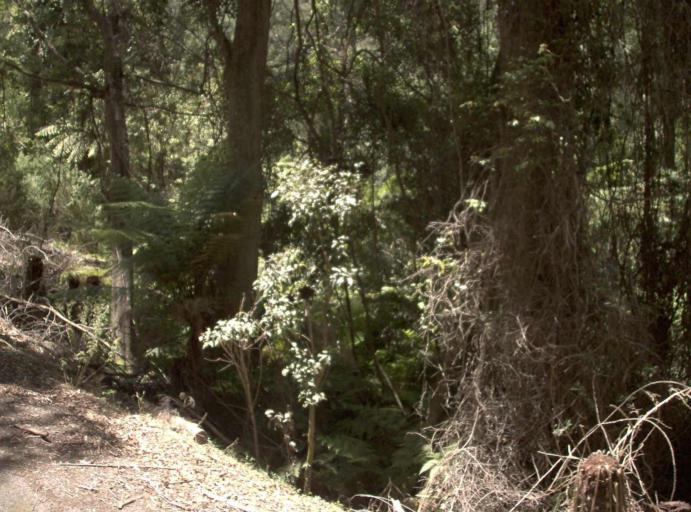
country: AU
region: New South Wales
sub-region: Bombala
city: Bombala
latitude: -37.4578
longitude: 148.9366
